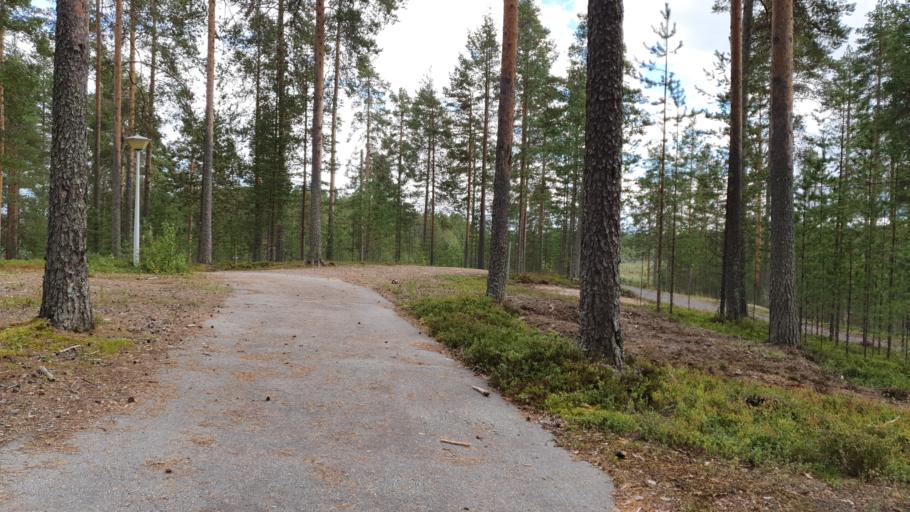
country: FI
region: Kainuu
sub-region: Kehys-Kainuu
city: Kuhmo
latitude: 64.1148
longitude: 29.5909
